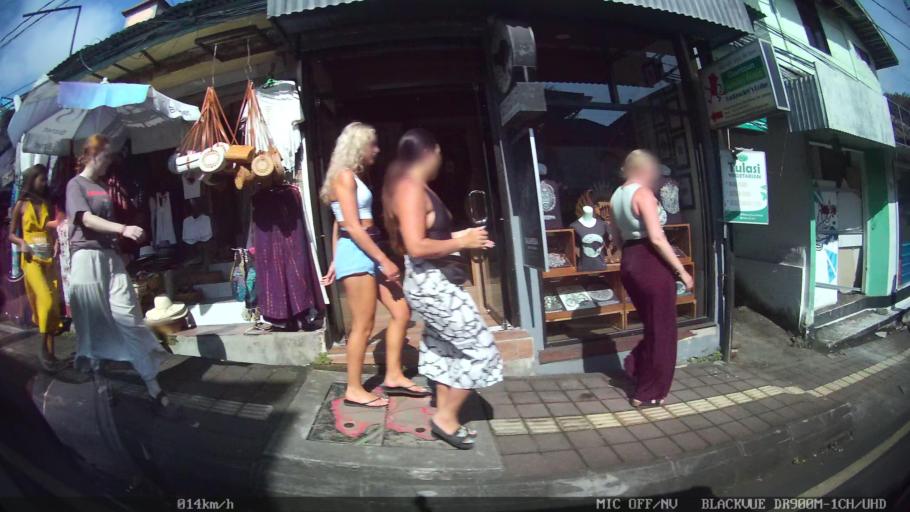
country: ID
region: Bali
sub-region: Kabupaten Gianyar
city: Ubud
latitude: -8.5168
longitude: 115.2601
